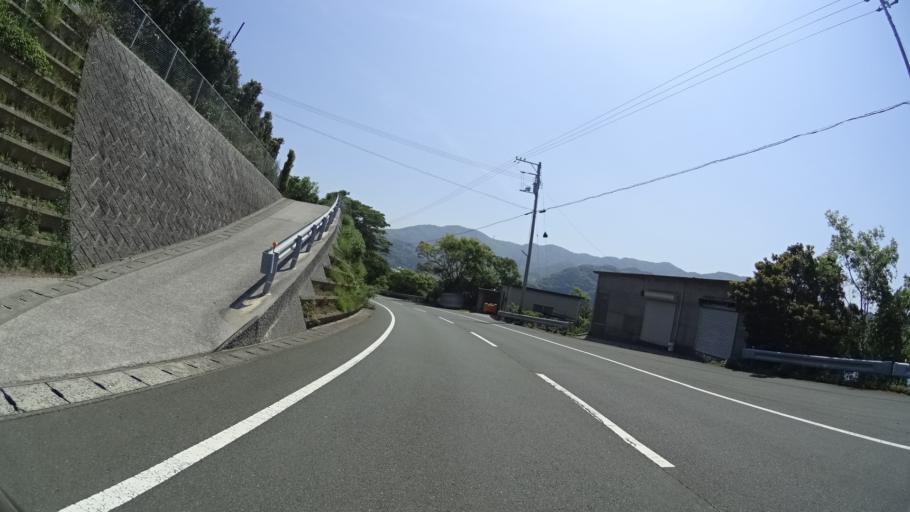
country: JP
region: Ehime
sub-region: Nishiuwa-gun
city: Ikata-cho
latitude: 33.3899
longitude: 132.1103
